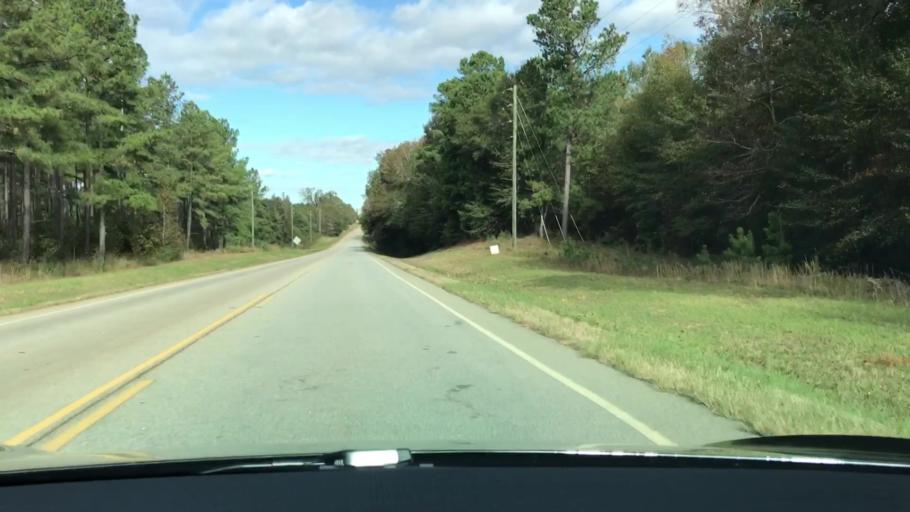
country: US
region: Georgia
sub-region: Jefferson County
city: Louisville
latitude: 33.0908
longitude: -82.4162
